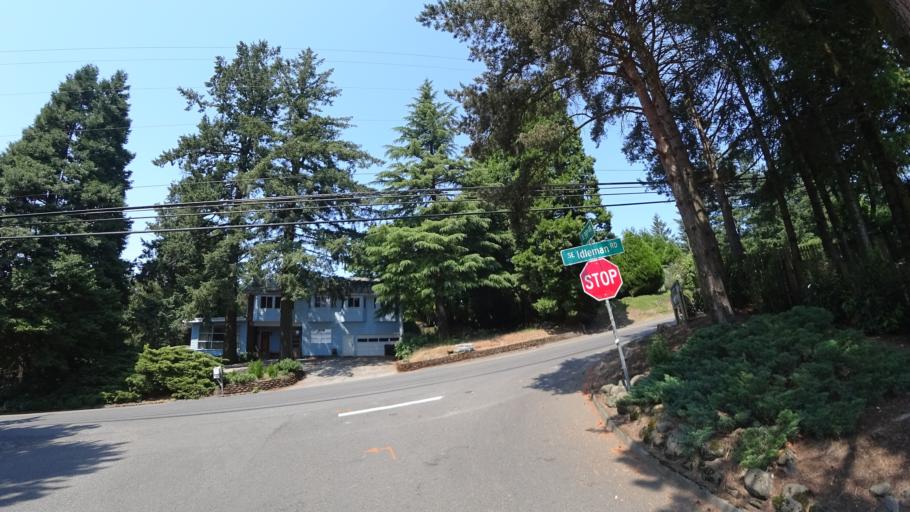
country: US
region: Oregon
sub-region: Multnomah County
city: Lents
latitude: 45.4503
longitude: -122.5617
